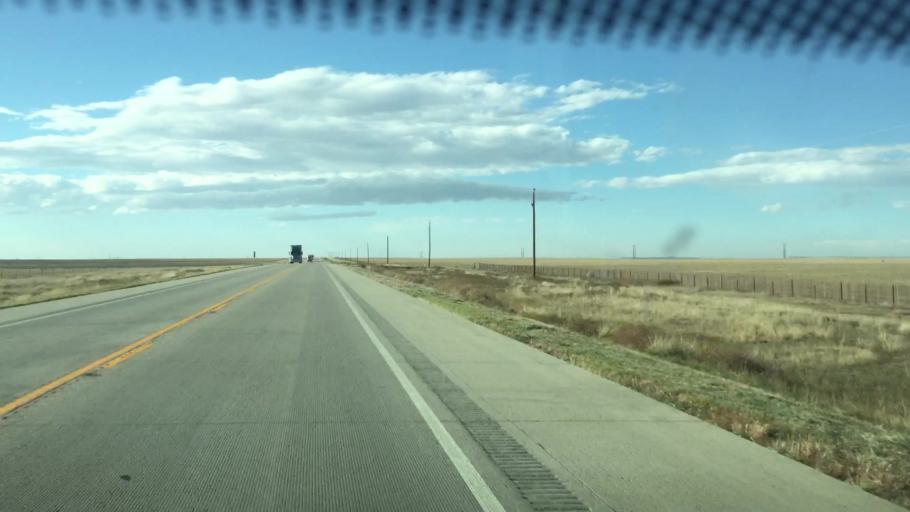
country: US
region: Colorado
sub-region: Lincoln County
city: Hugo
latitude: 39.0793
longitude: -103.3858
